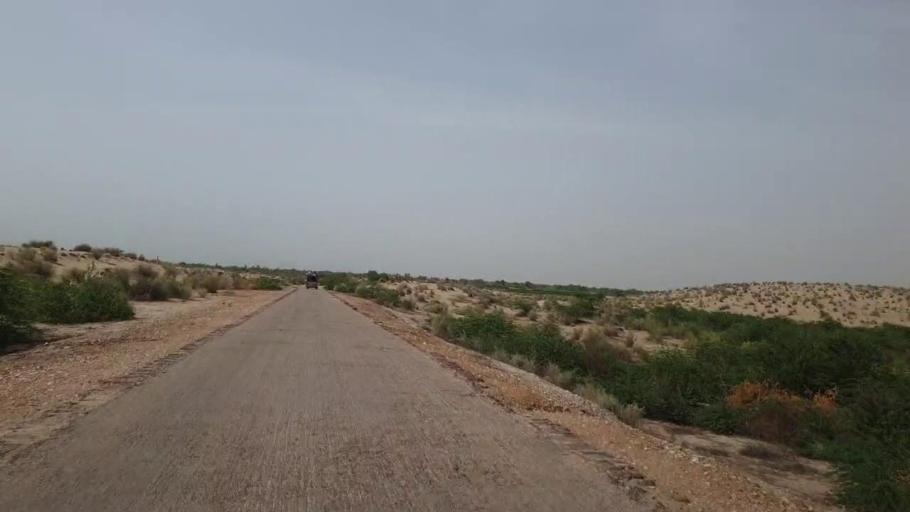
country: PK
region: Sindh
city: Bandhi
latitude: 26.5586
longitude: 68.3823
